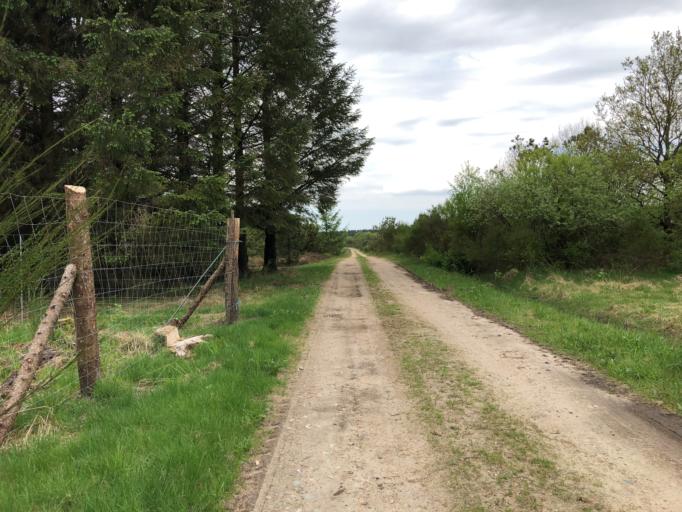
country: DK
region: Central Jutland
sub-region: Holstebro Kommune
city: Ulfborg
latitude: 56.2963
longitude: 8.4212
